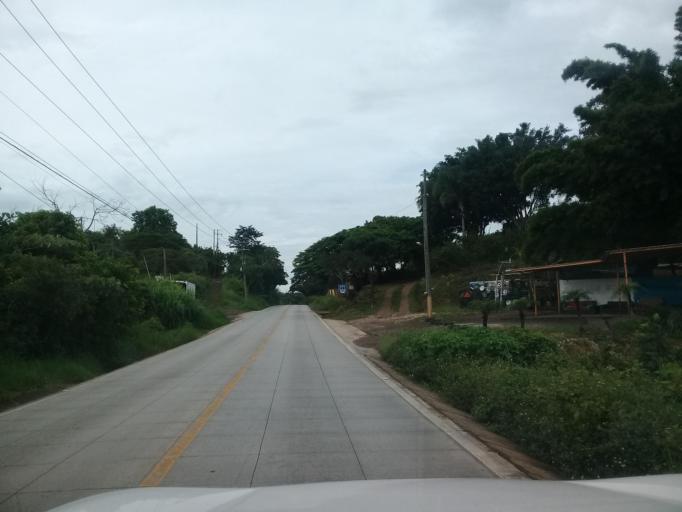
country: MX
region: Veracruz
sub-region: Emiliano Zapata
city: Jacarandas
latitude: 19.4841
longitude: -96.8575
